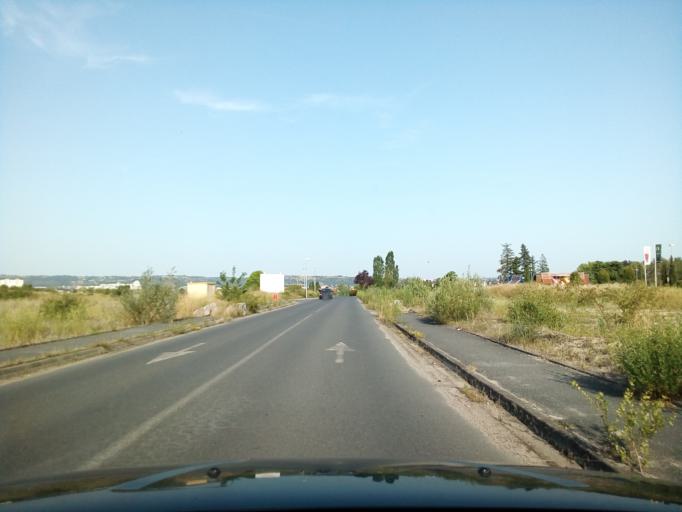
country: FR
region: Auvergne
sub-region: Departement de l'Allier
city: Domerat
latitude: 46.3393
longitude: 2.5638
